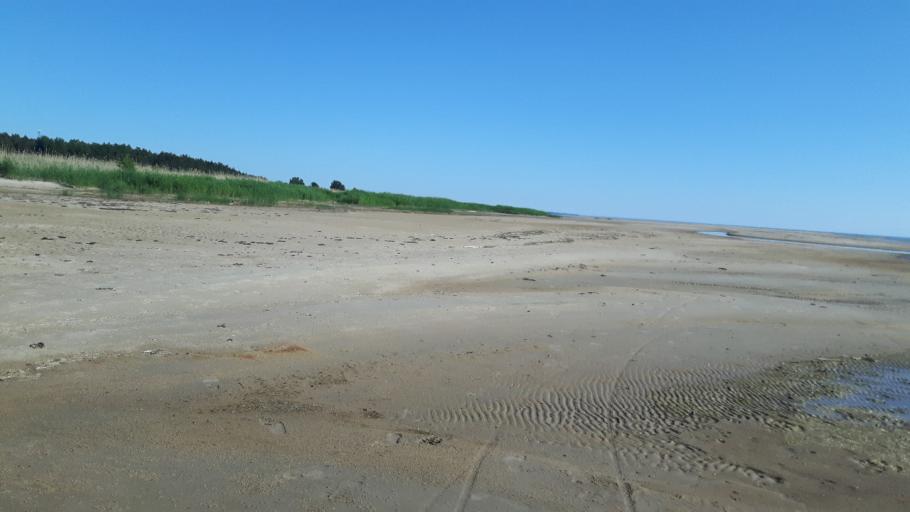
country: LV
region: Salacgrivas
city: Salacgriva
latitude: 57.7046
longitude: 24.3425
